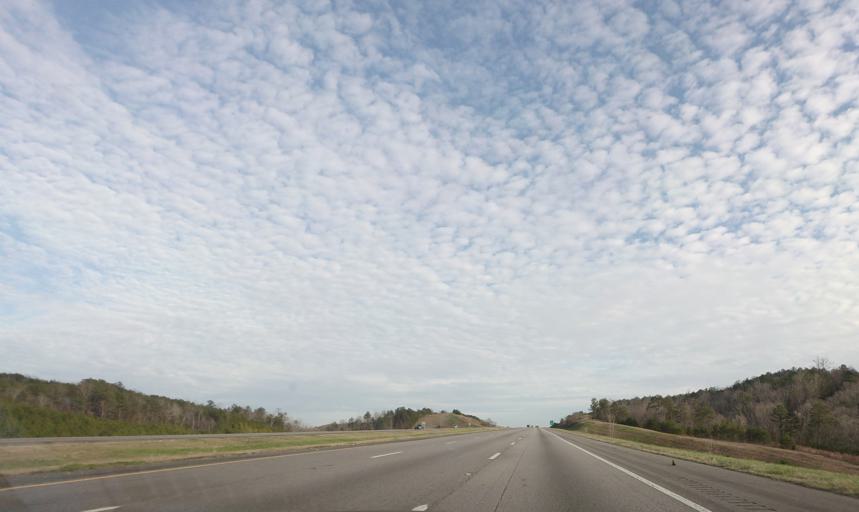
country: US
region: Alabama
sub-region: Walker County
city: Dora
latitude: 33.6842
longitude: -87.0998
